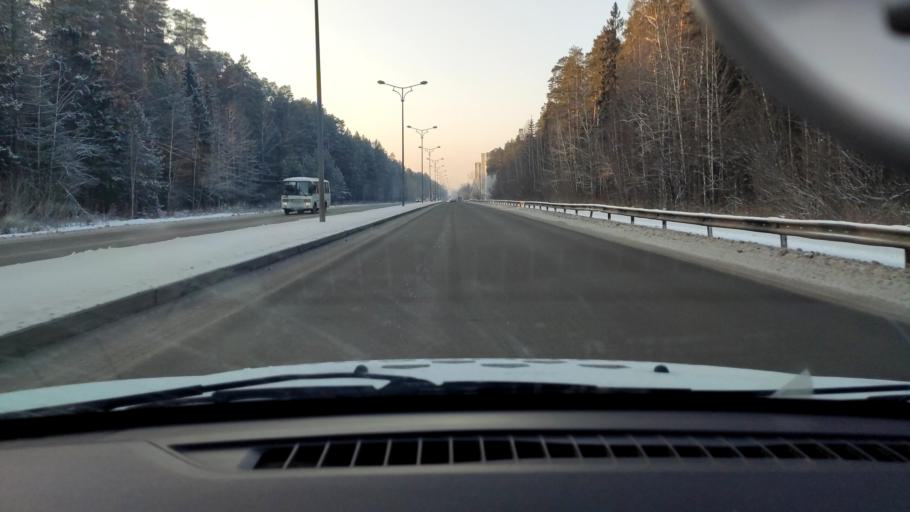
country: RU
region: Perm
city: Kondratovo
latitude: 58.0194
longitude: 55.9892
